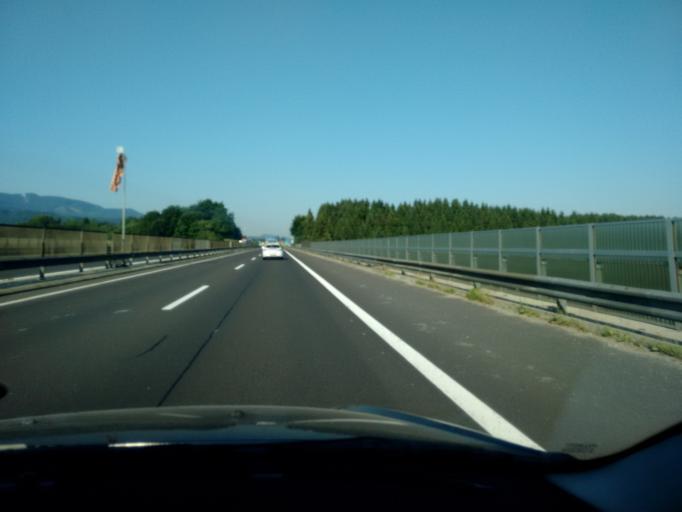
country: AT
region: Upper Austria
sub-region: Politischer Bezirk Vocklabruck
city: Attnang-Puchheim
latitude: 47.9612
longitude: 13.7460
